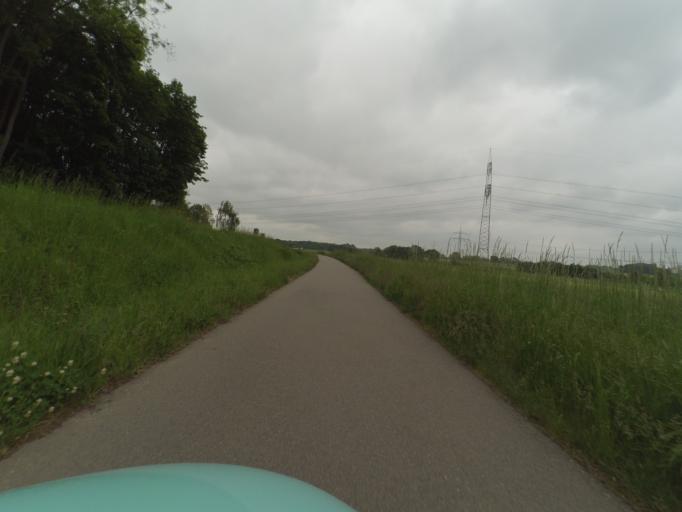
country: DE
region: Lower Saxony
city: Wendeburg
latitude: 52.3470
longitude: 10.3585
